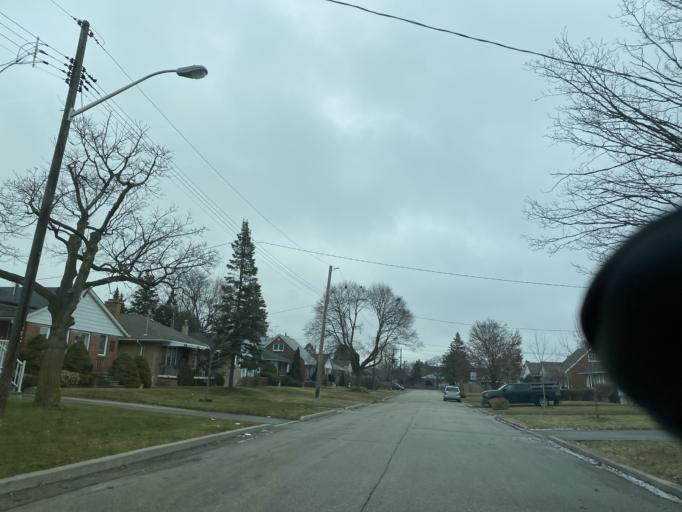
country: CA
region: Ontario
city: Scarborough
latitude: 43.7611
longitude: -79.3133
